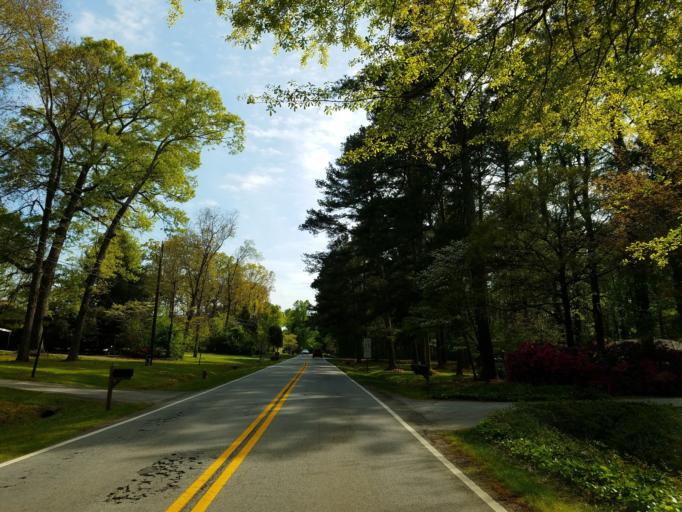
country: US
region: Georgia
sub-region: Douglas County
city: Lithia Springs
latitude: 33.7791
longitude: -84.6373
